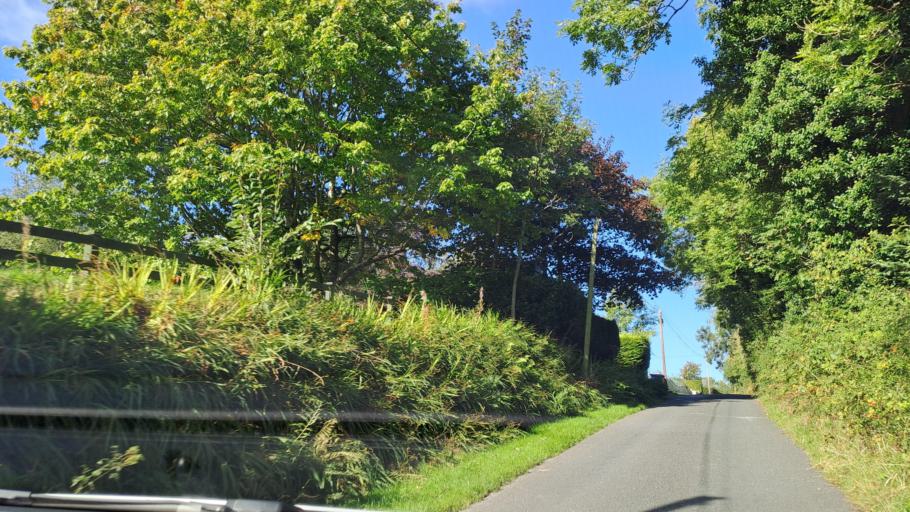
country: IE
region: Ulster
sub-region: County Monaghan
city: Carrickmacross
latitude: 53.9899
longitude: -6.7529
